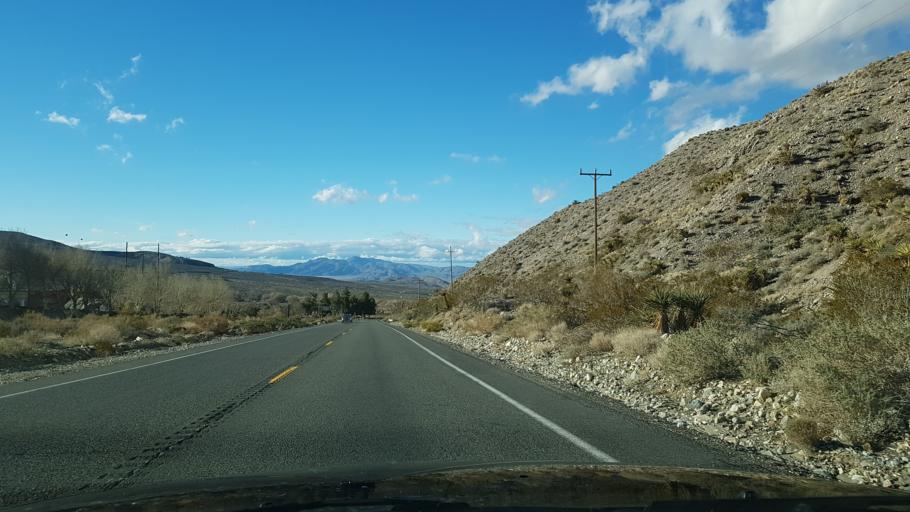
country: US
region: California
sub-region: San Bernardino County
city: Big Bear City
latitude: 34.3553
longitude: -116.8501
